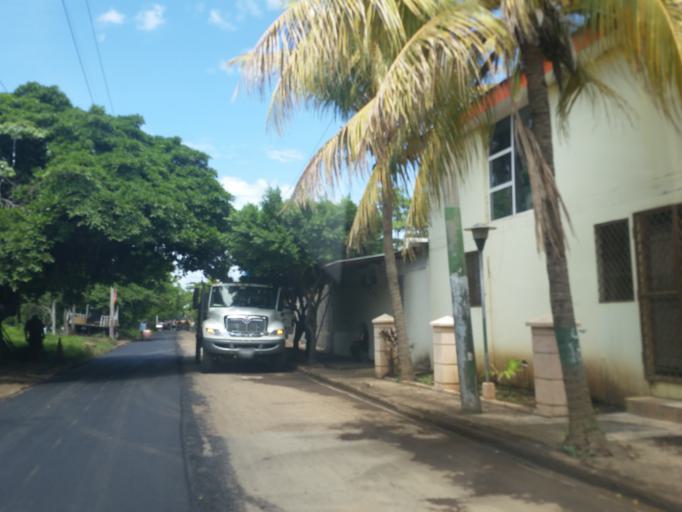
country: NI
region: Managua
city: Managua
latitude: 12.1258
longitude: -86.2877
